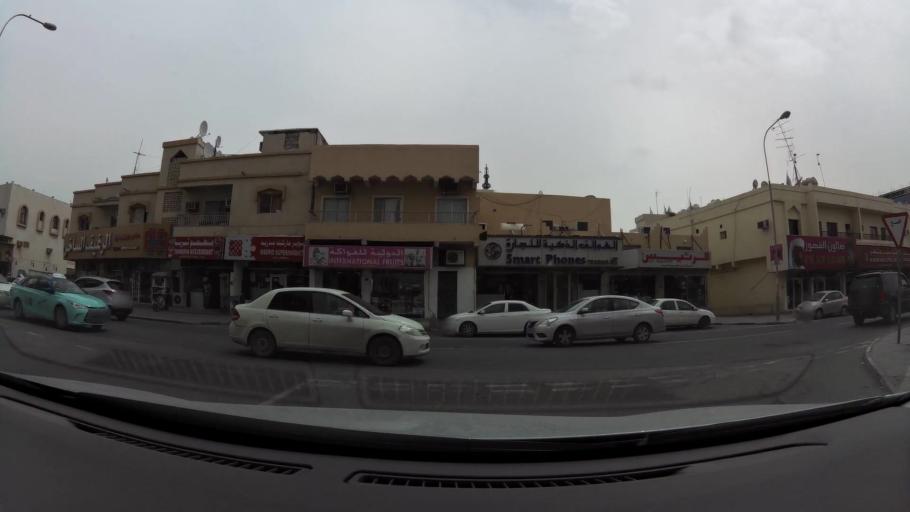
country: QA
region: Baladiyat ad Dawhah
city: Doha
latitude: 25.2506
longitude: 51.5519
